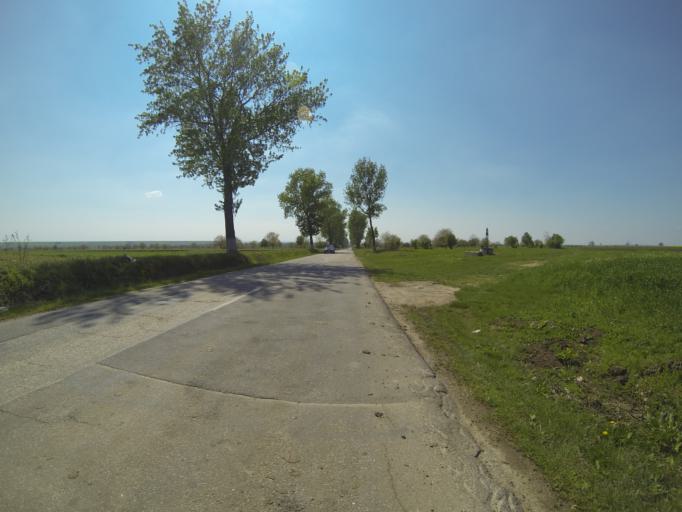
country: RO
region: Dolj
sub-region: Comuna Caraula
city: Caraula
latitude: 44.1985
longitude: 23.2720
